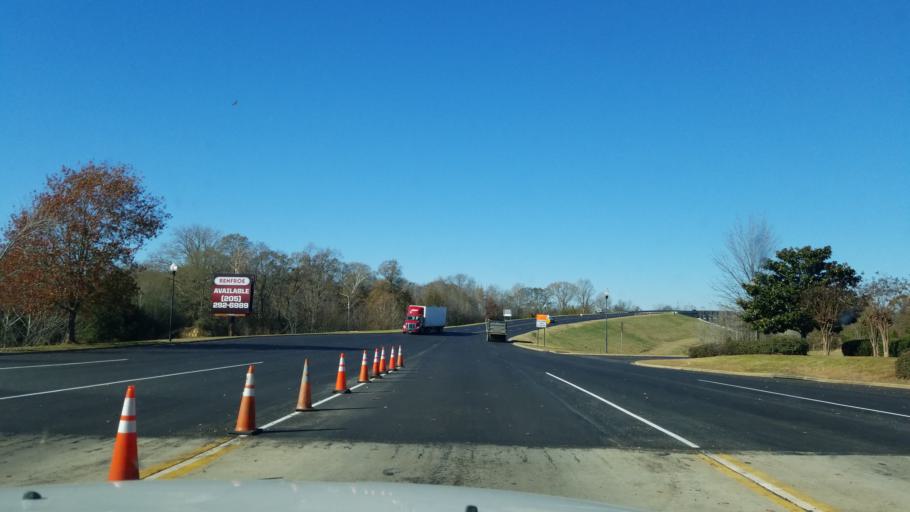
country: US
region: Alabama
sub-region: Tuscaloosa County
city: Tuscaloosa
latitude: 33.1945
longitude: -87.6244
